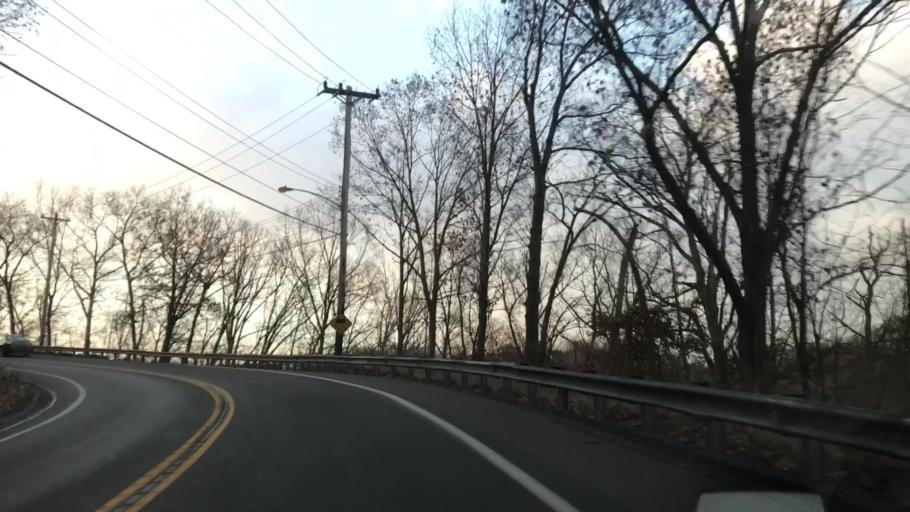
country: US
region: Pennsylvania
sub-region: Allegheny County
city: Carnot-Moon
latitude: 40.5270
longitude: -80.2295
